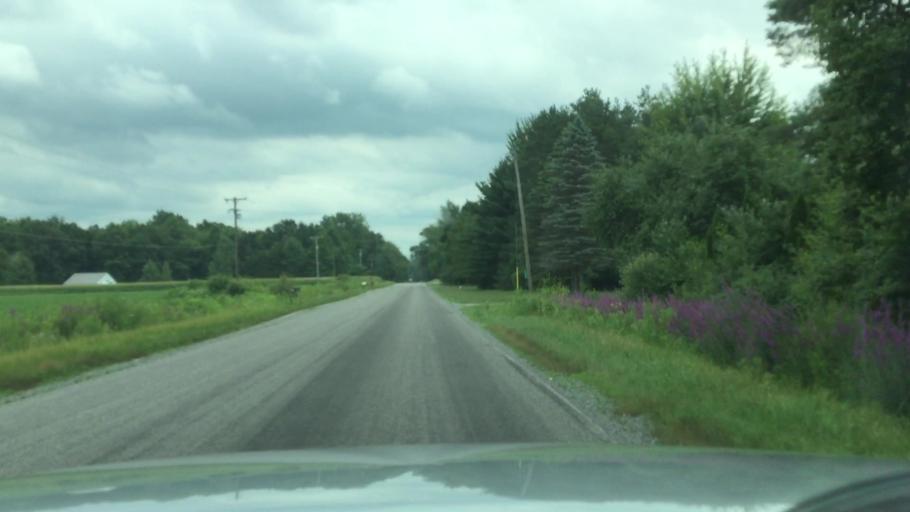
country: US
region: Michigan
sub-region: Saginaw County
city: Bridgeport
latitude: 43.3220
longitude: -83.8844
